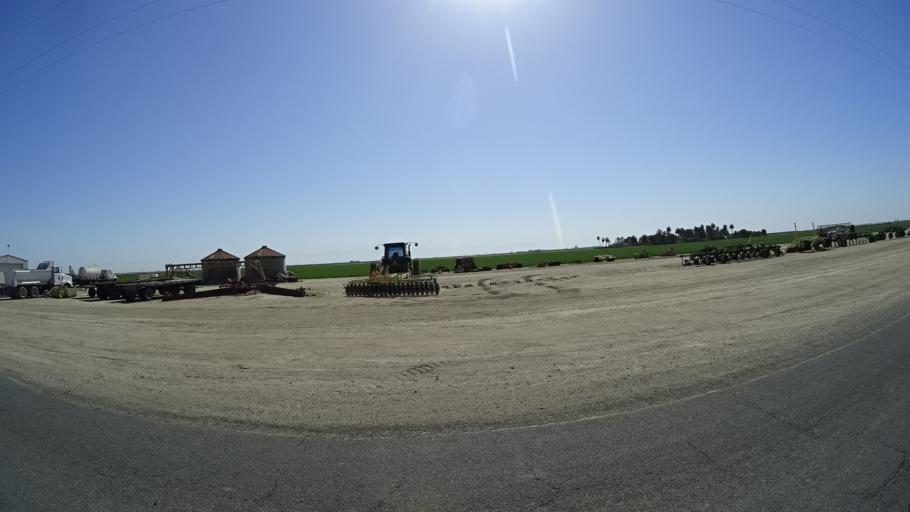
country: US
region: California
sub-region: Kings County
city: Home Garden
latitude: 36.2350
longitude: -119.5472
